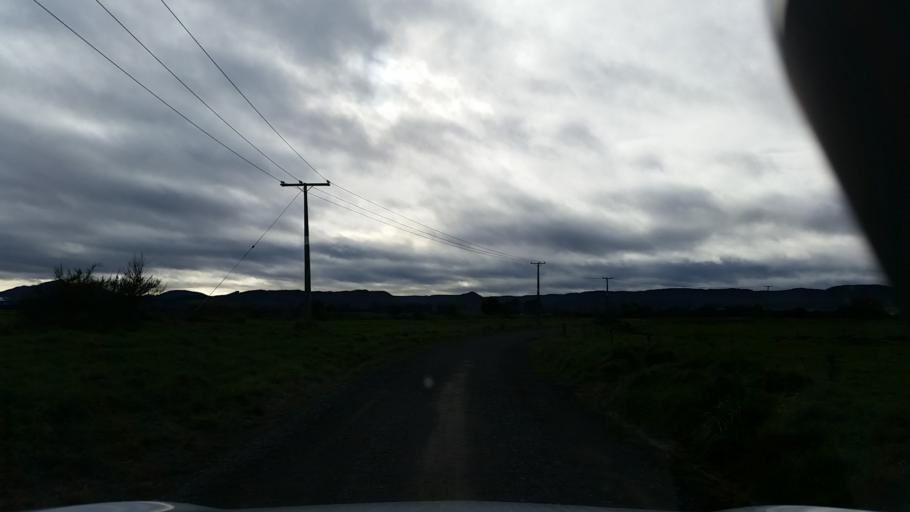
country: NZ
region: Bay of Plenty
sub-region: Rotorua District
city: Rotorua
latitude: -38.4150
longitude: 176.3520
